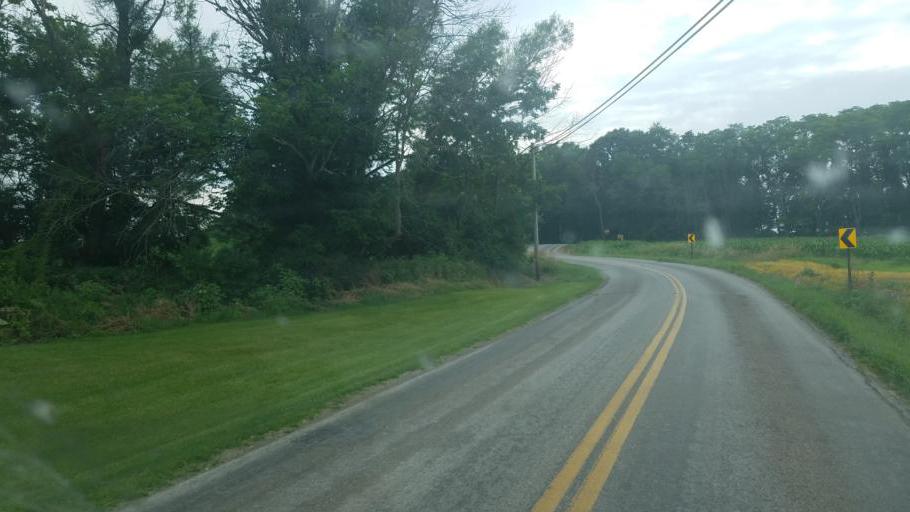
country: US
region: Ohio
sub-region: Wayne County
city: Apple Creek
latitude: 40.7557
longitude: -81.8237
